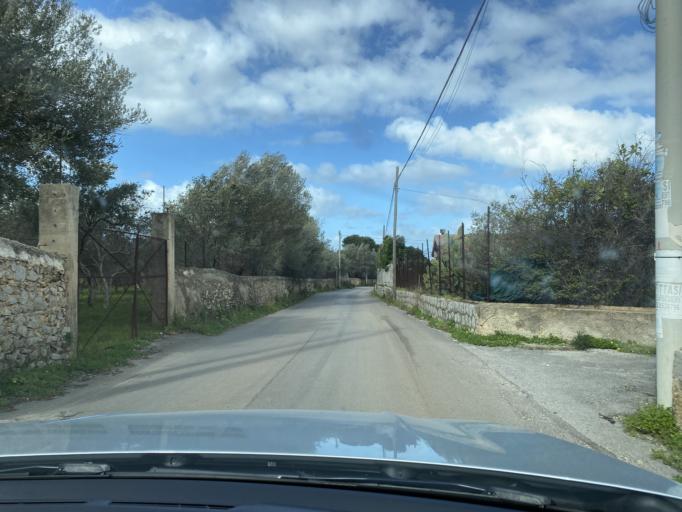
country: IT
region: Sicily
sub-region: Palermo
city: Carini
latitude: 38.1523
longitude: 13.1678
